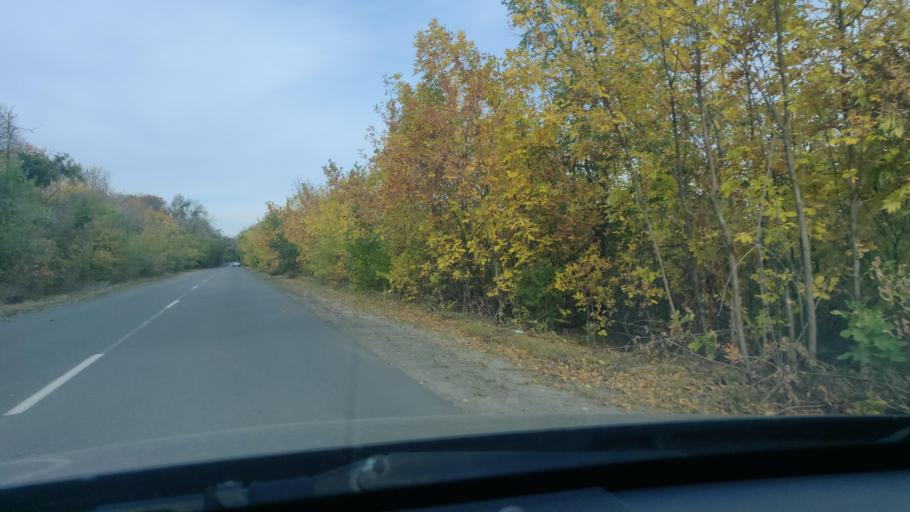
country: RU
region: Rostov
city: Ust'-Donetskiy
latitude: 47.6511
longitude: 40.8911
